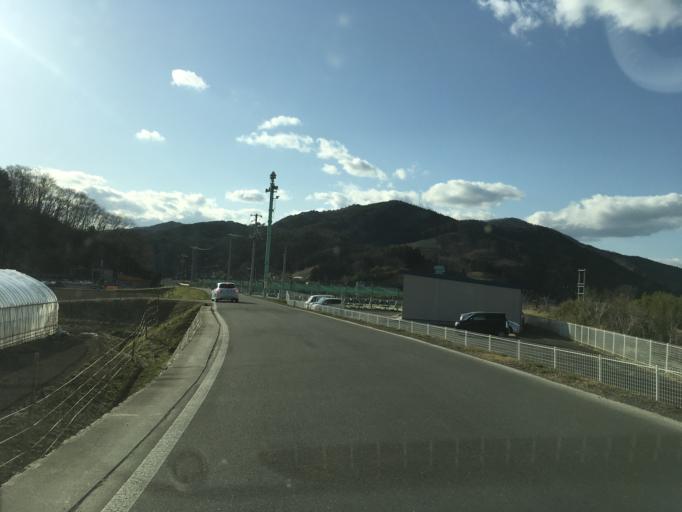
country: JP
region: Iwate
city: Ofunato
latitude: 39.0304
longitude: 141.6065
